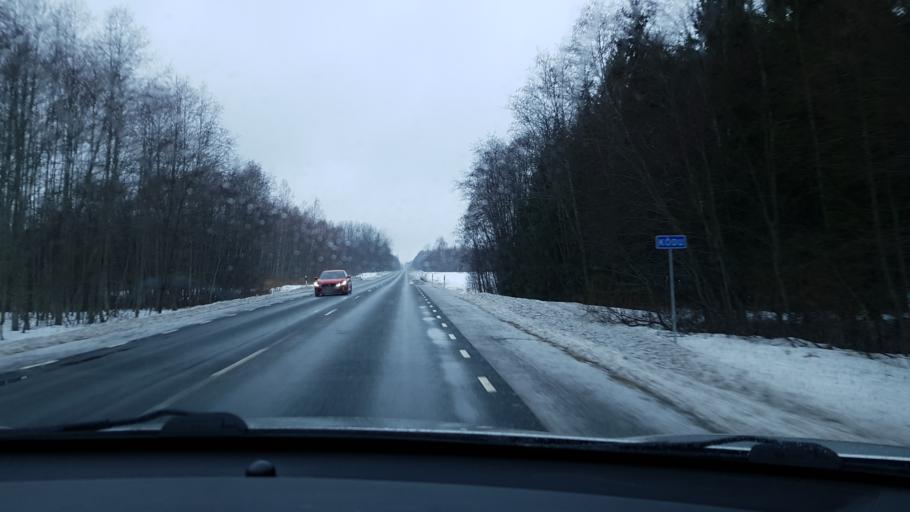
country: EE
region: Jaervamaa
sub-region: Tueri vald
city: Sarevere
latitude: 58.8038
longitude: 25.2213
